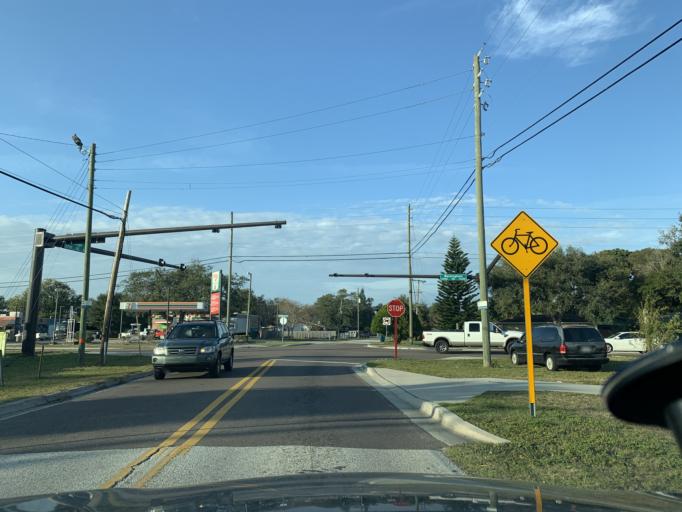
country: US
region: Florida
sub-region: Pinellas County
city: Ridgecrest
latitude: 27.8798
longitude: -82.7978
